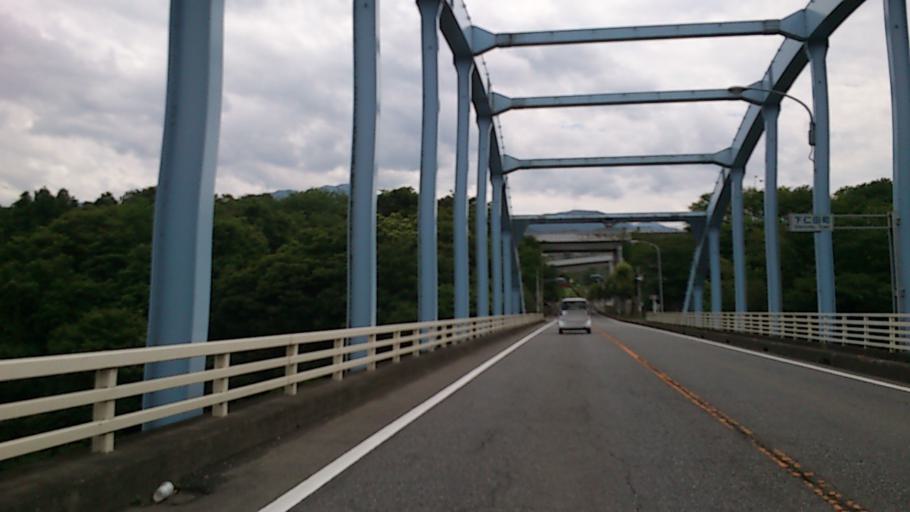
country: JP
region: Gunma
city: Tomioka
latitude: 36.2377
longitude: 138.8232
